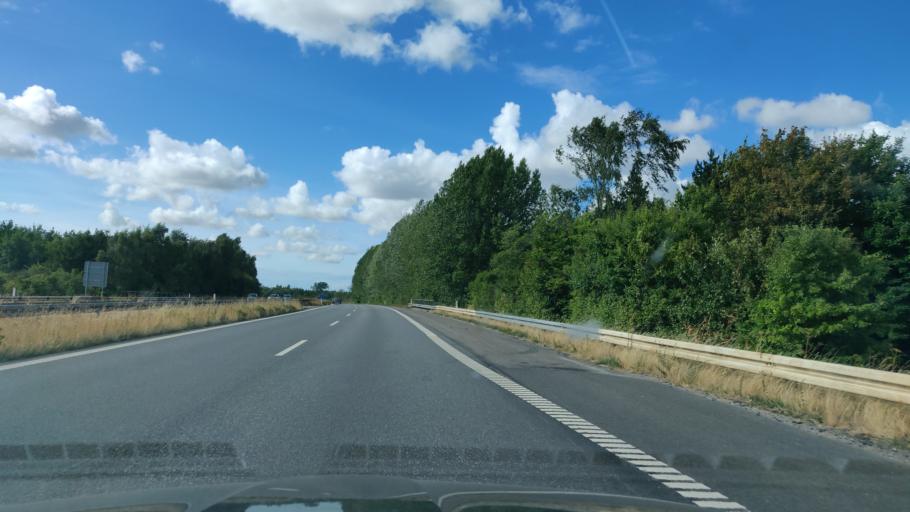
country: DK
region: Zealand
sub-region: Holbaek Kommune
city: Vipperod
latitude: 55.6705
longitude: 11.7552
